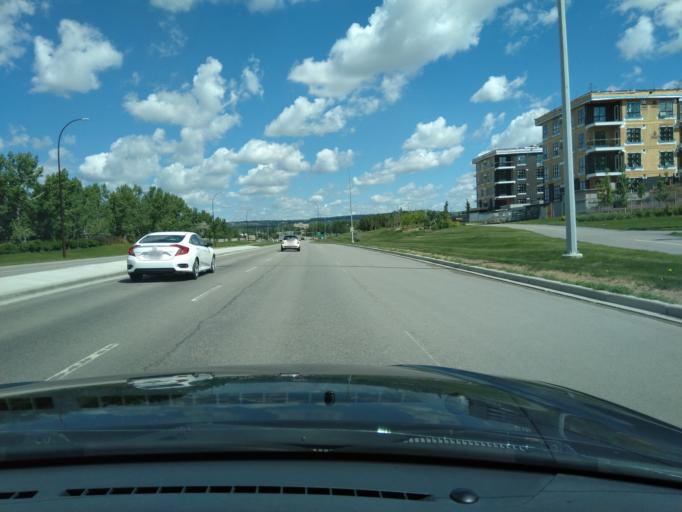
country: CA
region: Alberta
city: Calgary
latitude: 51.0773
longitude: -114.1520
